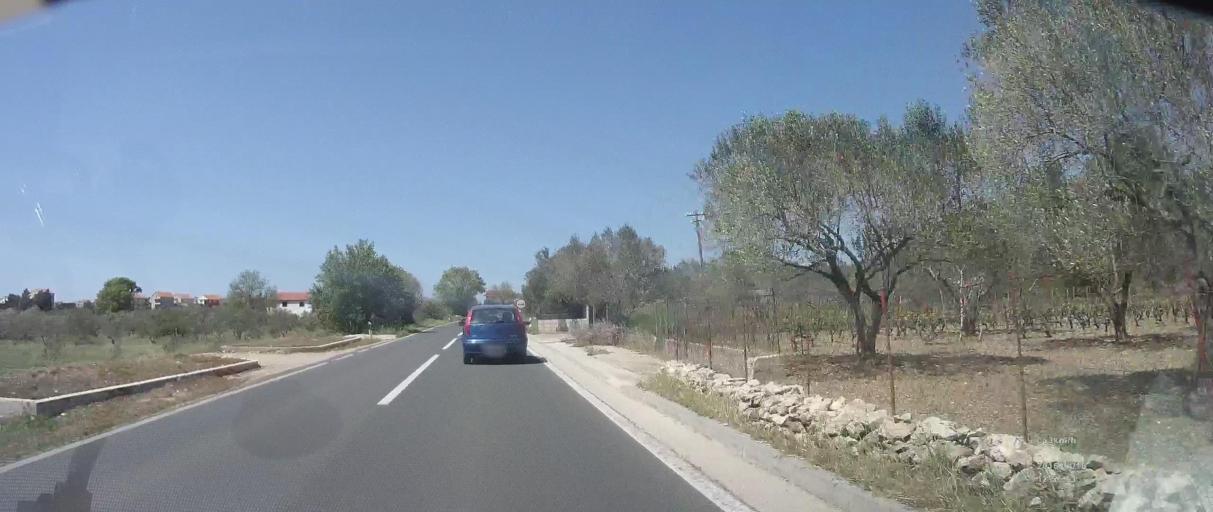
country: HR
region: Sibensko-Kniniska
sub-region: Grad Sibenik
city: Brodarica
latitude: 43.7025
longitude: 15.9371
